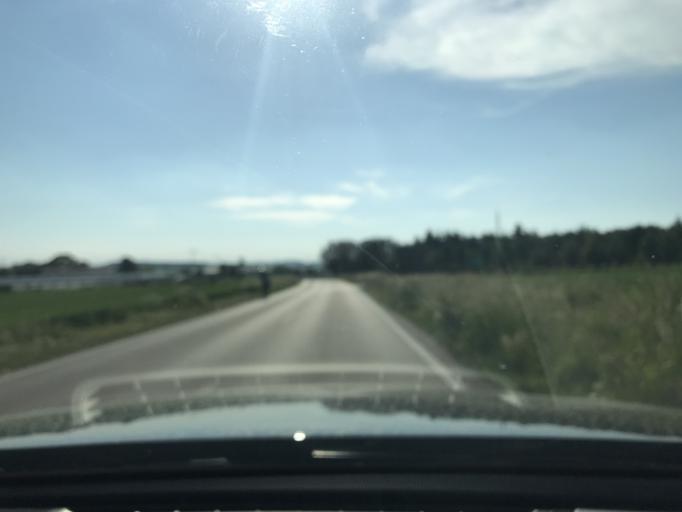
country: DE
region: Baden-Wuerttemberg
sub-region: Regierungsbezirk Stuttgart
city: Schwaikheim
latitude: 48.8912
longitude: 9.3355
